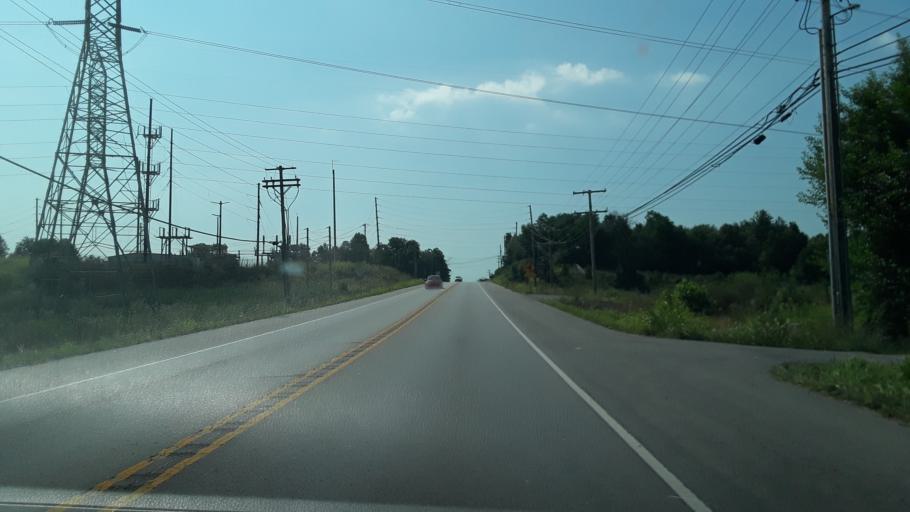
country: US
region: Indiana
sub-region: Clark County
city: Sellersburg
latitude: 38.4034
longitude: -85.7869
